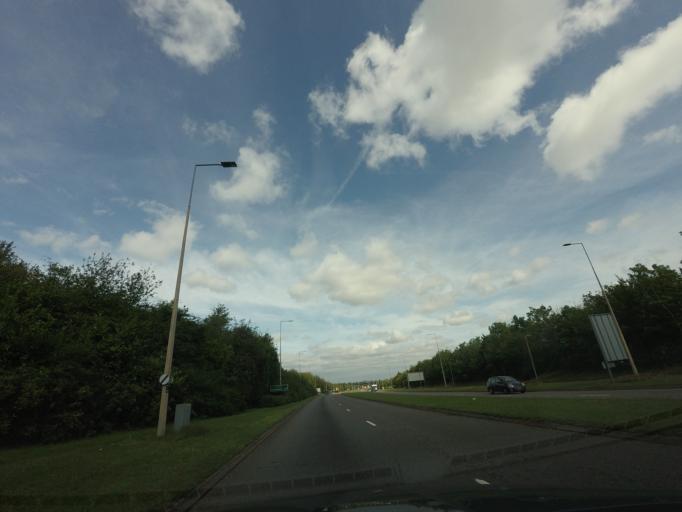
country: GB
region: England
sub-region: Milton Keynes
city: Simpson
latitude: 52.0272
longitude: -0.6908
